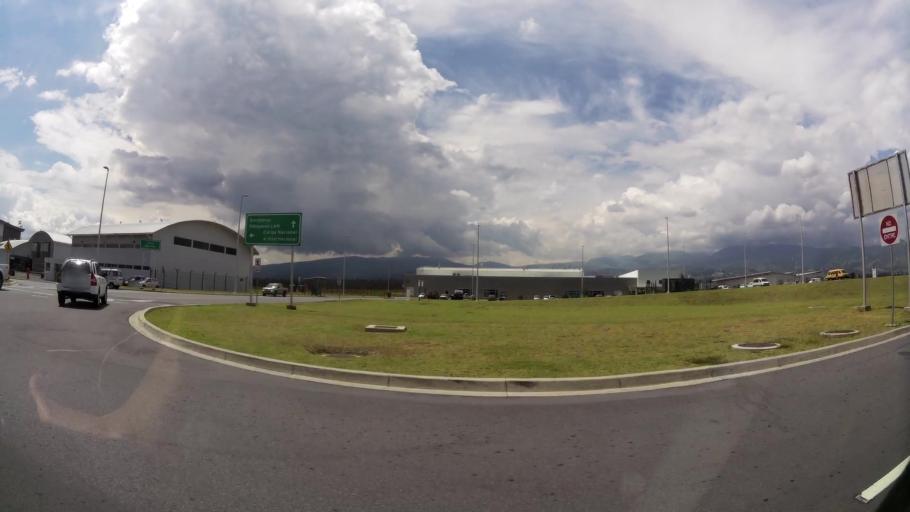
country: EC
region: Pichincha
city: Quito
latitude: -0.1328
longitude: -78.3587
